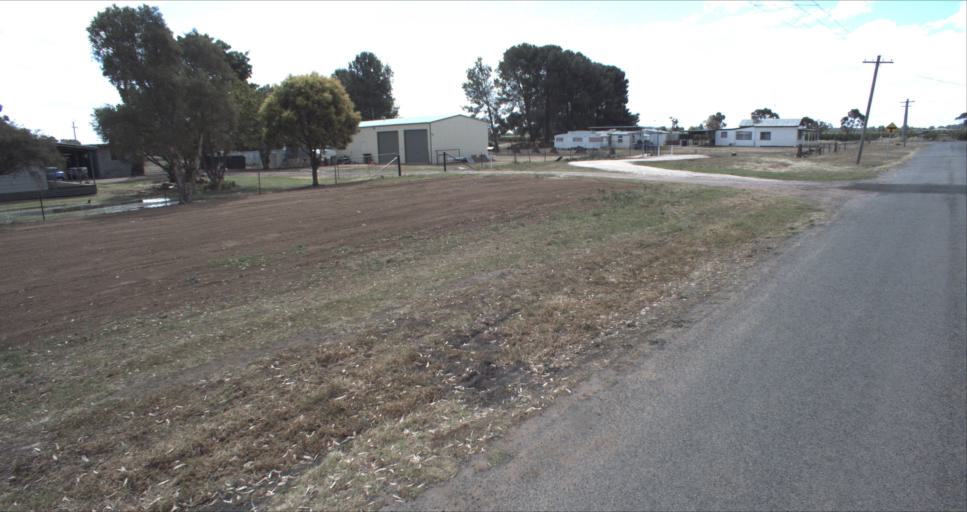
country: AU
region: New South Wales
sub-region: Leeton
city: Leeton
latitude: -34.5924
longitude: 146.4065
